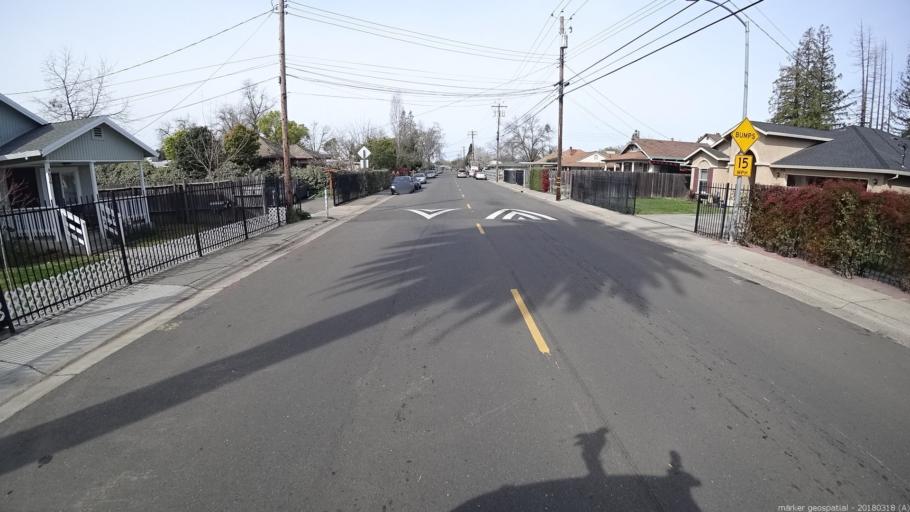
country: US
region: California
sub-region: Sacramento County
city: Parkway
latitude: 38.5352
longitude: -121.4522
